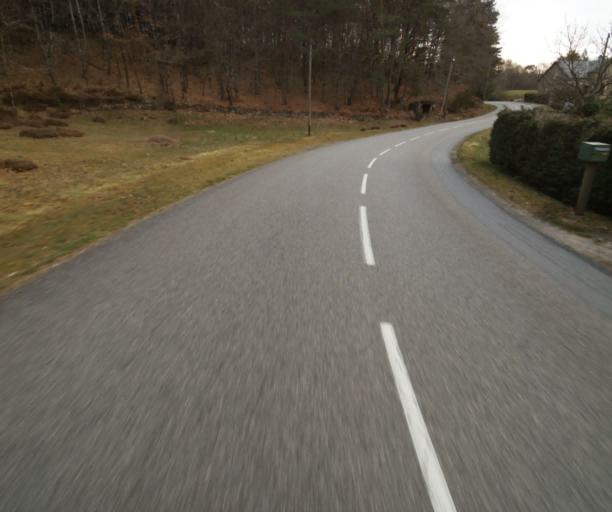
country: FR
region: Limousin
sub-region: Departement de la Correze
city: Correze
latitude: 45.4279
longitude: 1.8491
